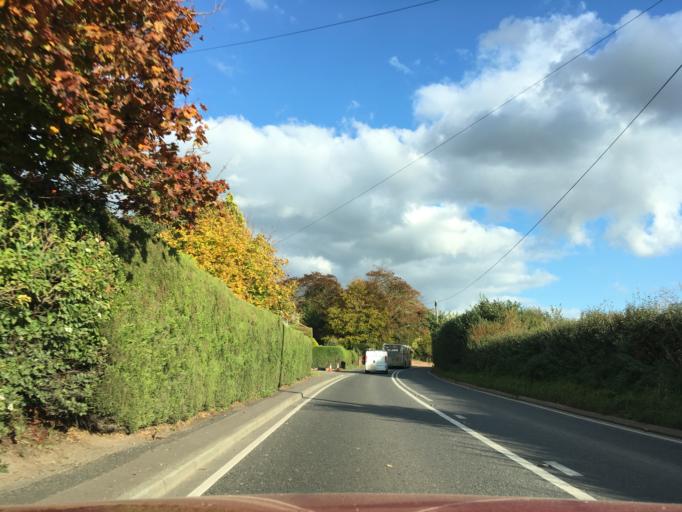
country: GB
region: England
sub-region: Herefordshire
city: Credenhill
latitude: 52.0727
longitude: -2.7860
